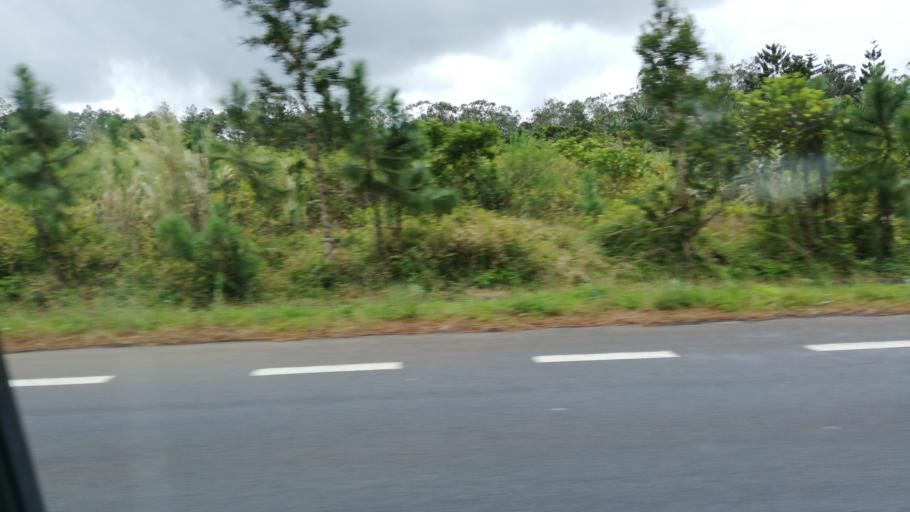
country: MU
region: Plaines Wilhems
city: Curepipe
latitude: -20.2916
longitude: 57.5455
